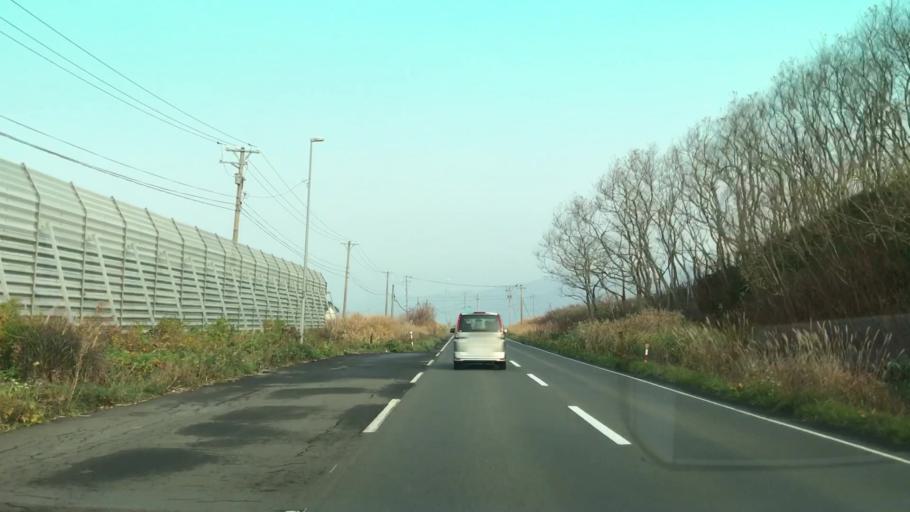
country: JP
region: Hokkaido
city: Ishikari
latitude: 43.3691
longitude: 141.4269
